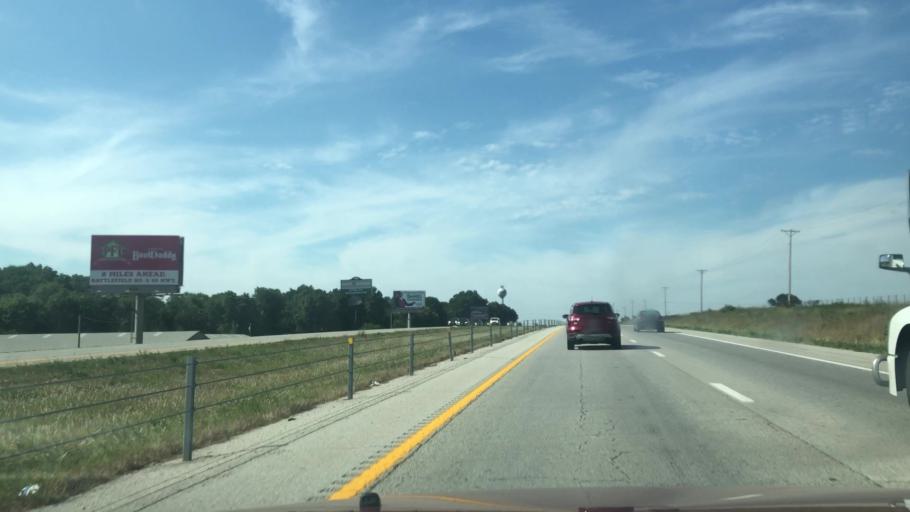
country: US
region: Missouri
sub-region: Christian County
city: Ozark
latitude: 37.0423
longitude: -93.2270
